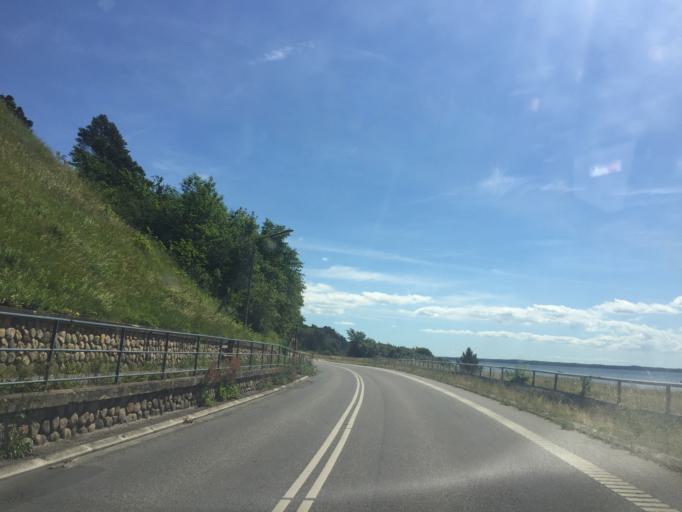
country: DK
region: Capital Region
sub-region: Halsnaes Kommune
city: Frederiksvaerk
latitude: 55.9592
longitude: 12.0197
